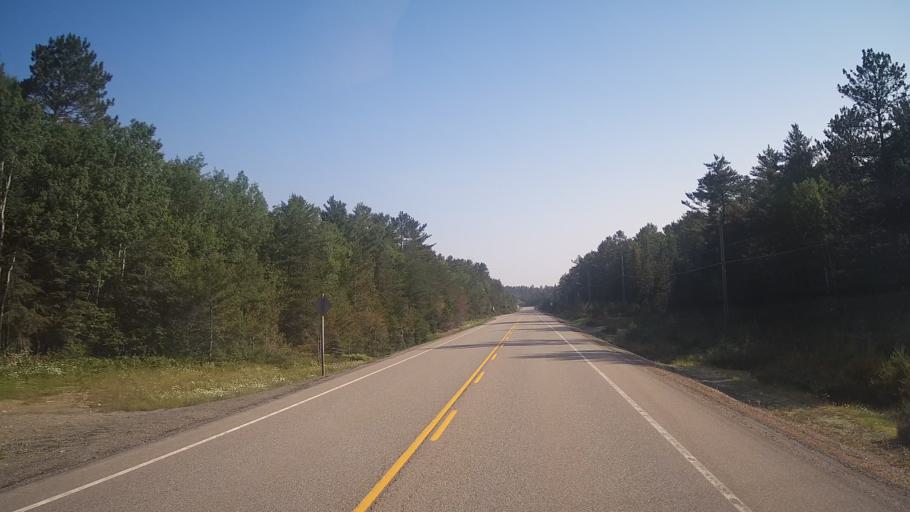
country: CA
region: Ontario
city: Rayside-Balfour
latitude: 46.7493
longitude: -81.6008
